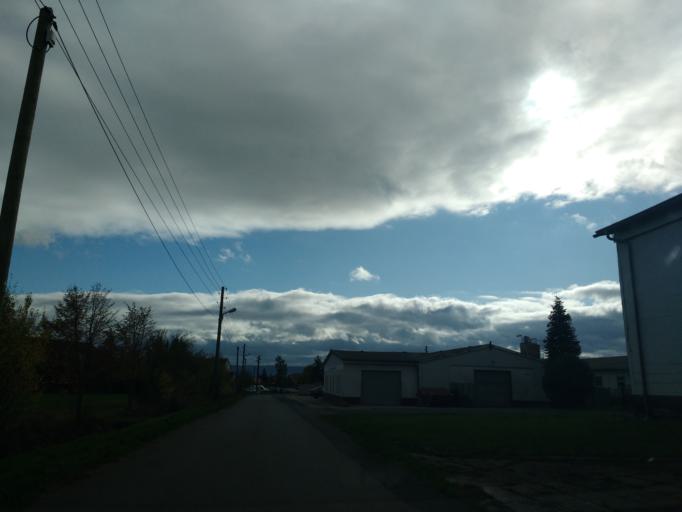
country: DE
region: Thuringia
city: Buhla
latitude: 51.4187
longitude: 10.4261
